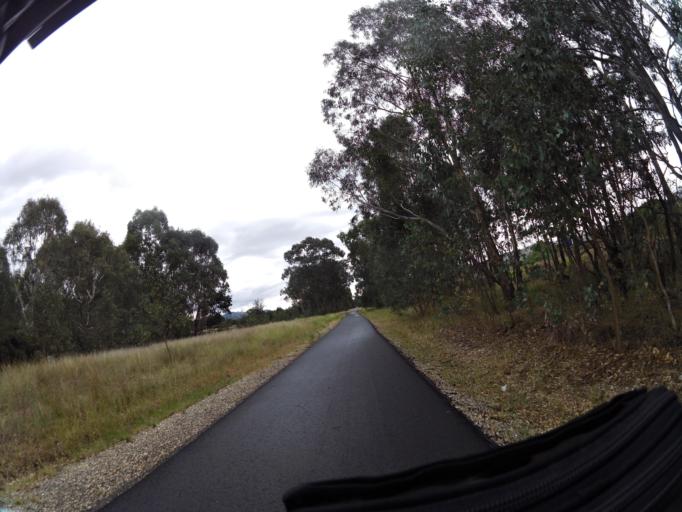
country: AU
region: Victoria
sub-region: Wodonga
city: Wodonga
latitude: -36.1399
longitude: 146.9101
